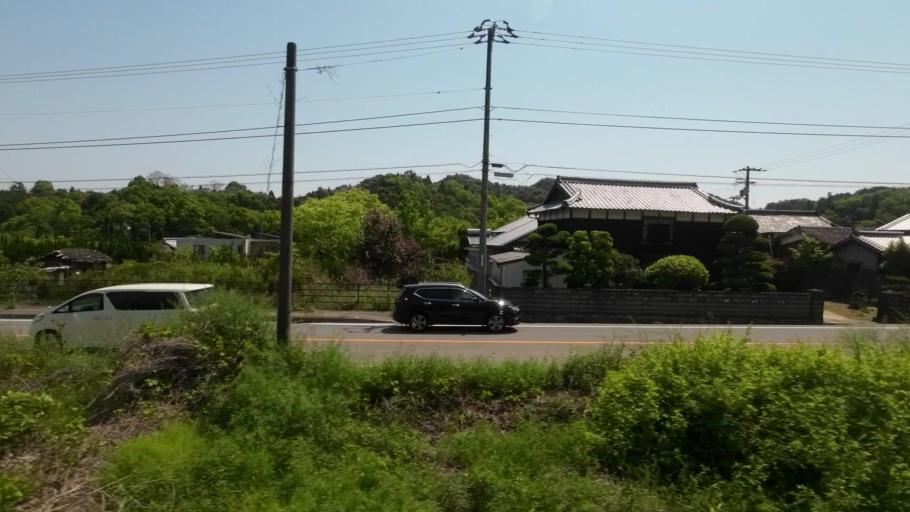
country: JP
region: Ehime
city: Saijo
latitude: 33.9853
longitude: 133.0524
